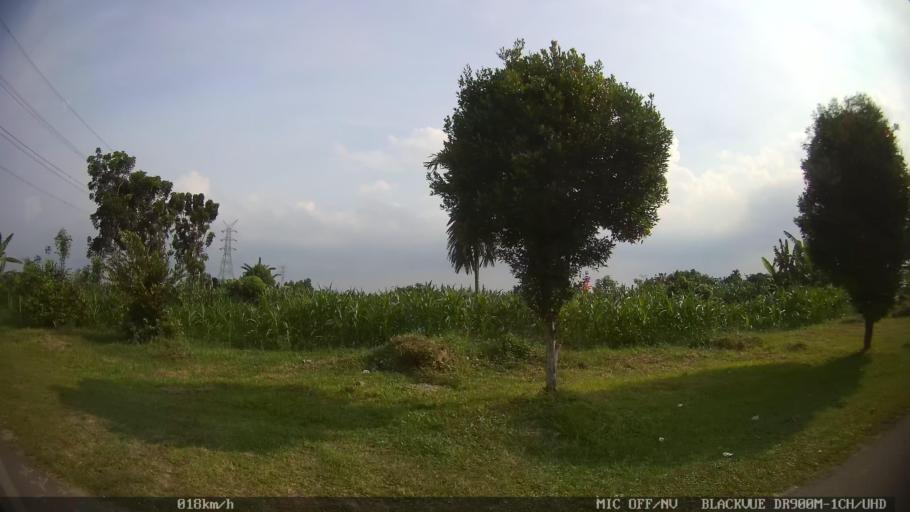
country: ID
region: North Sumatra
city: Binjai
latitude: 3.6030
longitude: 98.5100
